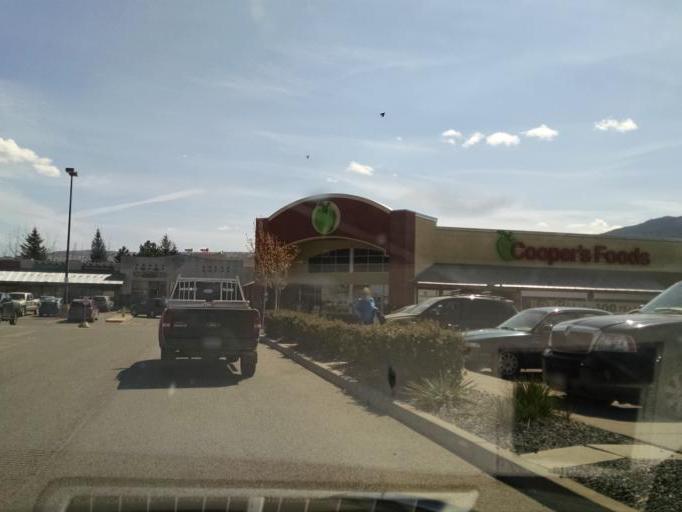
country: CA
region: British Columbia
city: Merritt
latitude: 50.1077
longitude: -120.7880
